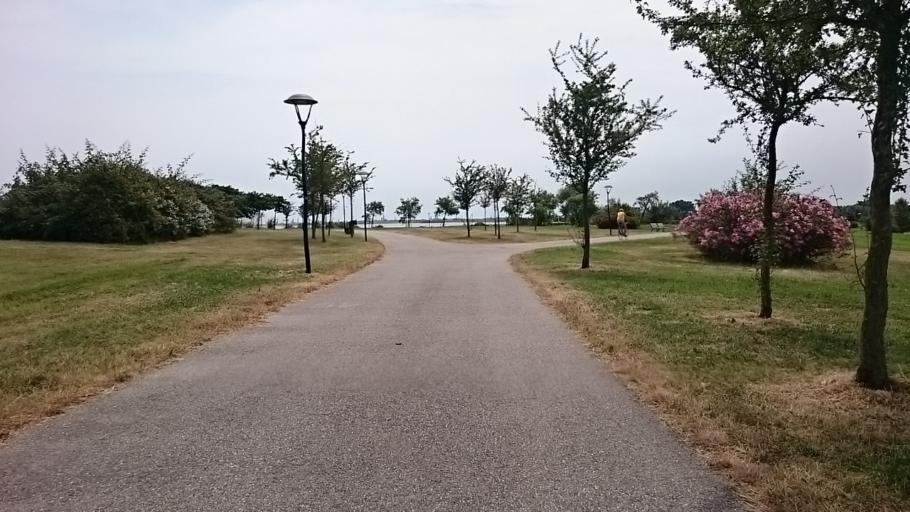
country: IT
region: Veneto
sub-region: Provincia di Venezia
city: Campalto
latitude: 45.4741
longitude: 12.2767
